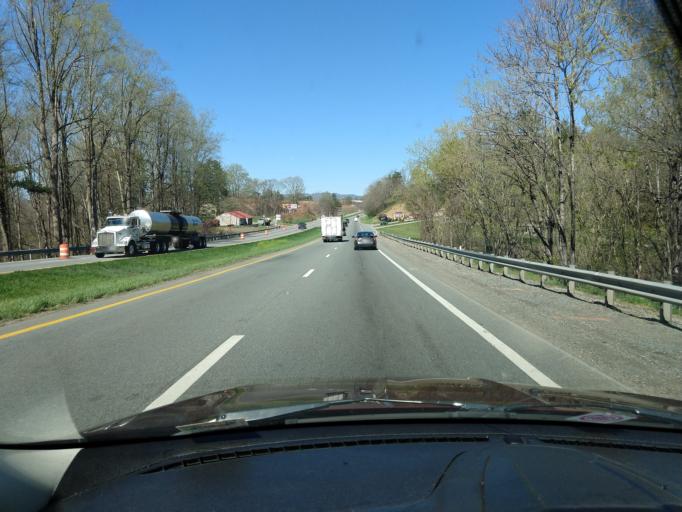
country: US
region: Virginia
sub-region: Franklin County
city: Rocky Mount
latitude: 37.0728
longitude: -79.9019
